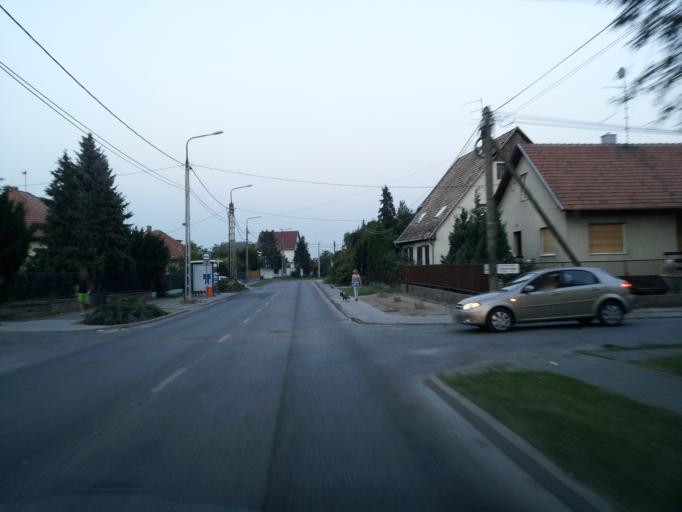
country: HU
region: Budapest
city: Budapest XXII. keruelet
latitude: 47.4239
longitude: 19.0245
